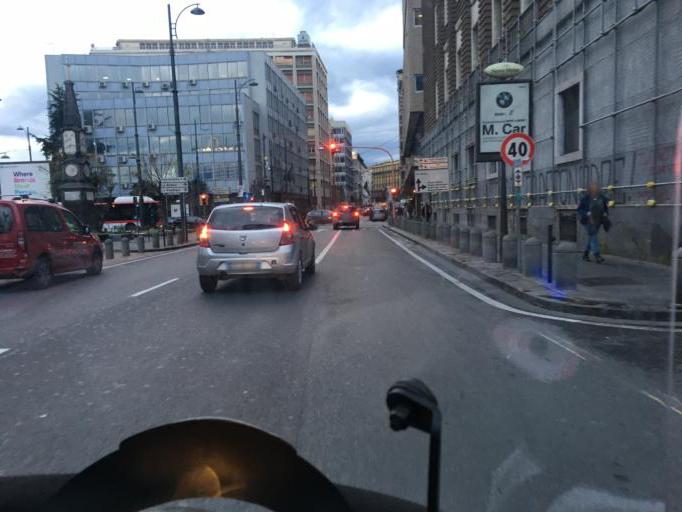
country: IT
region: Campania
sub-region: Provincia di Napoli
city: Napoli
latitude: 40.8429
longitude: 14.2574
